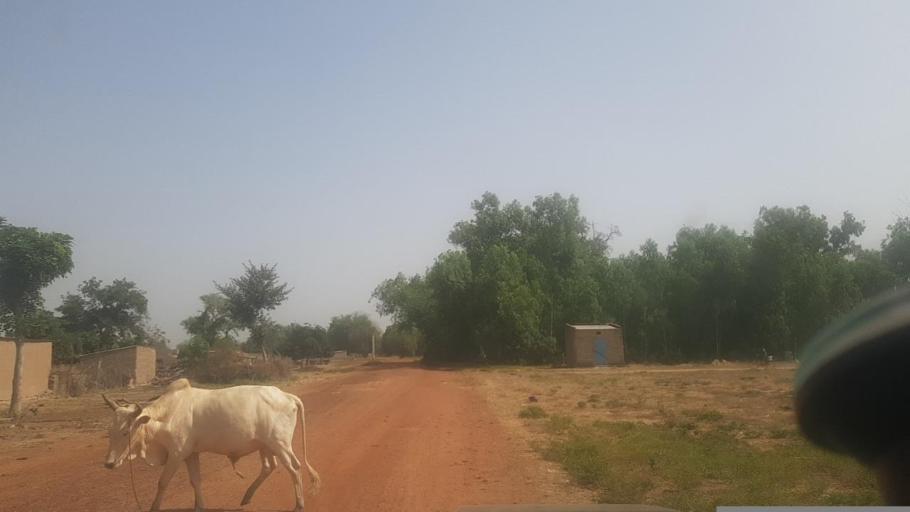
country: ML
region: Segou
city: Bla
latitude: 12.9127
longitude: -6.2458
